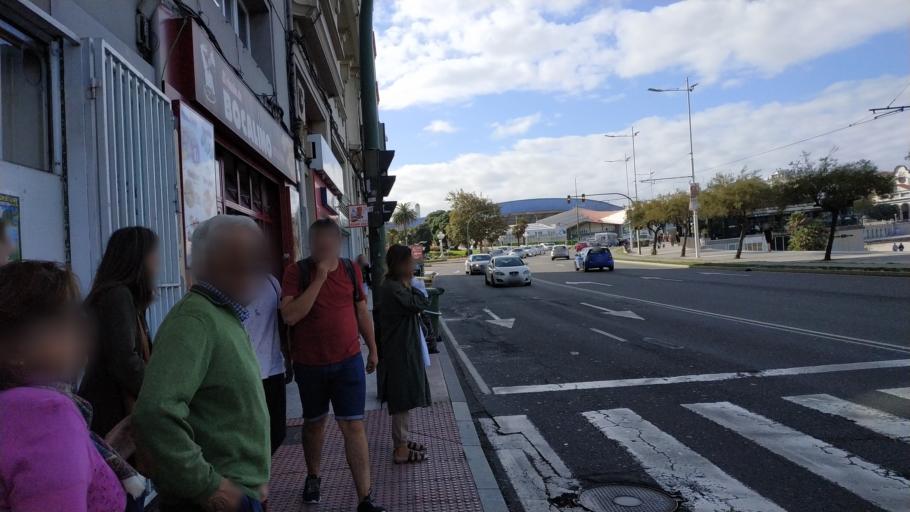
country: ES
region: Galicia
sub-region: Provincia da Coruna
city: A Coruna
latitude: 43.3680
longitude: -8.4125
